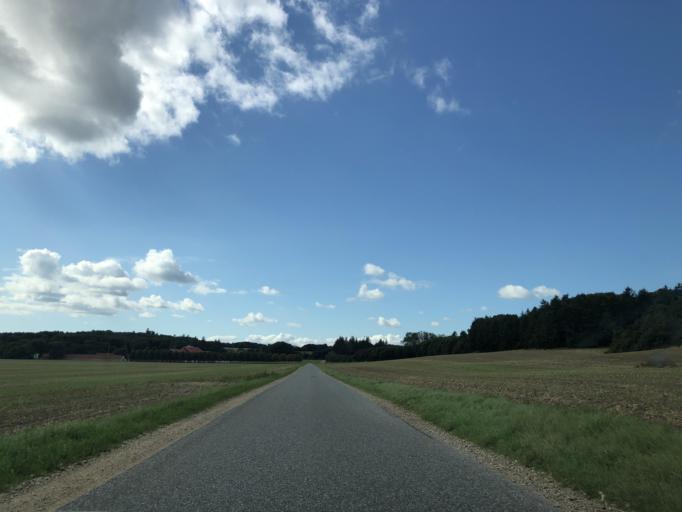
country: DK
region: Central Jutland
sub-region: Viborg Kommune
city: Viborg
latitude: 56.5699
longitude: 9.3344
